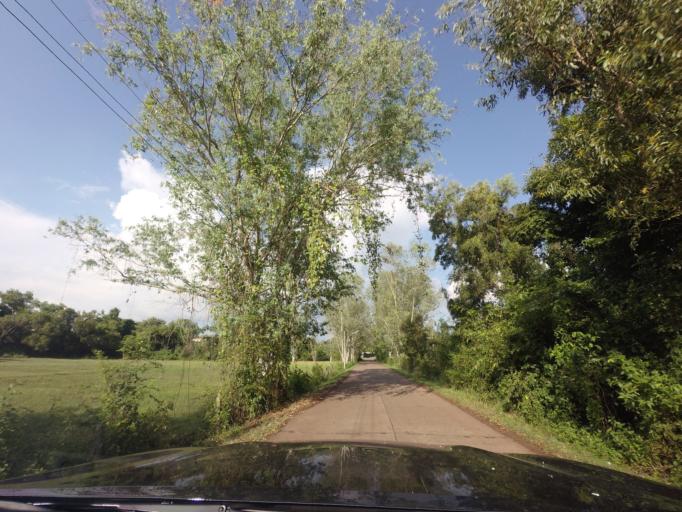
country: TH
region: Nong Khai
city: Nong Khai
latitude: 17.8857
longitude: 102.7748
